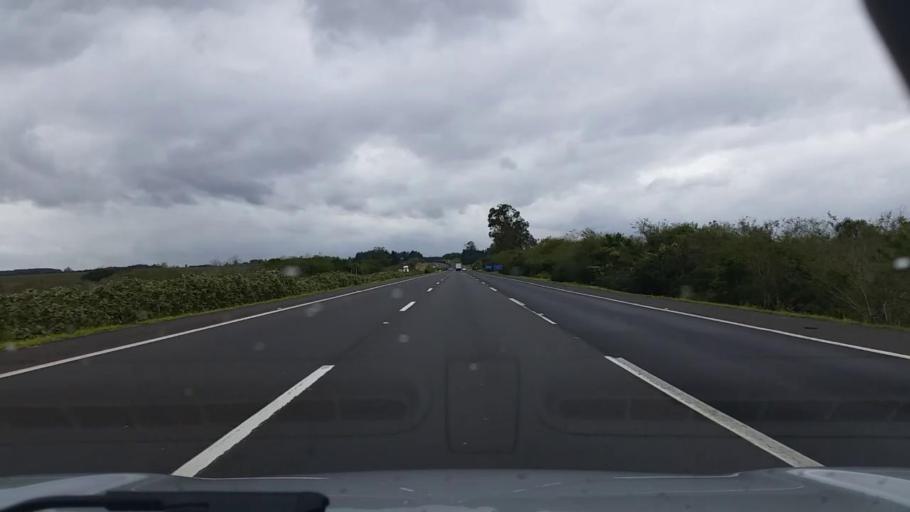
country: BR
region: Rio Grande do Sul
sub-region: Gravatai
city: Gravatai
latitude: -29.9213
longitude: -50.8415
